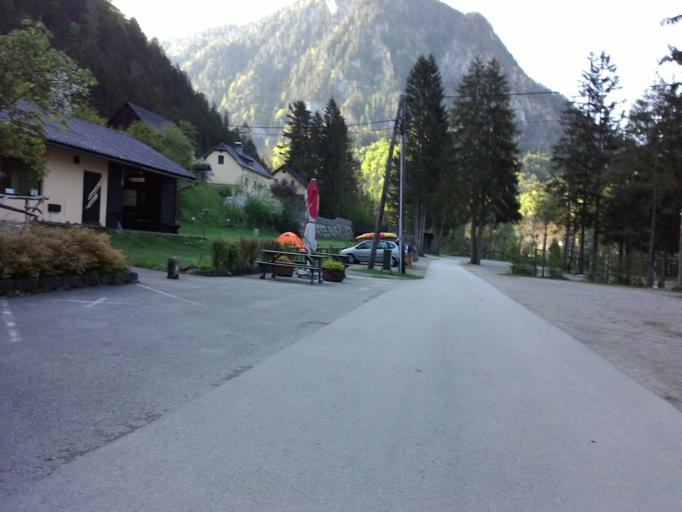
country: AT
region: Styria
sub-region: Politischer Bezirk Liezen
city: Wildalpen
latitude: 47.6657
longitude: 14.9875
